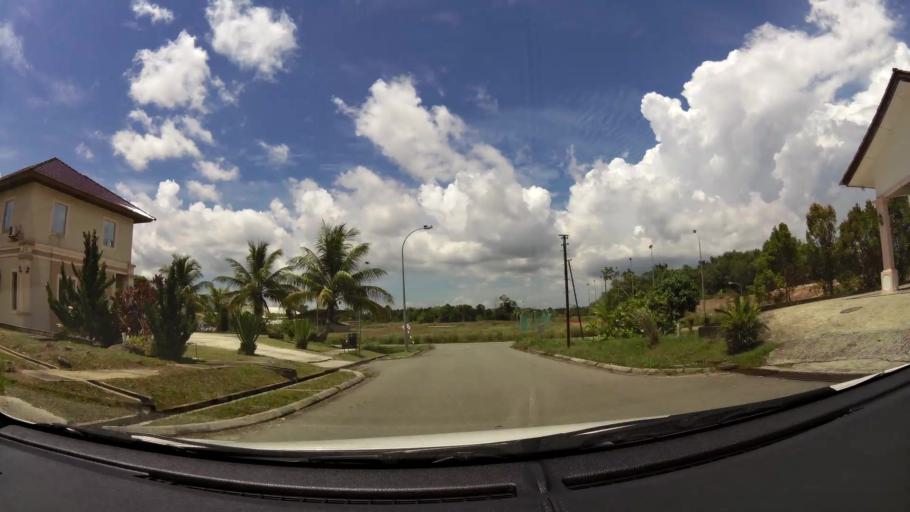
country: BN
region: Brunei and Muara
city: Bandar Seri Begawan
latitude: 4.9668
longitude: 114.9006
